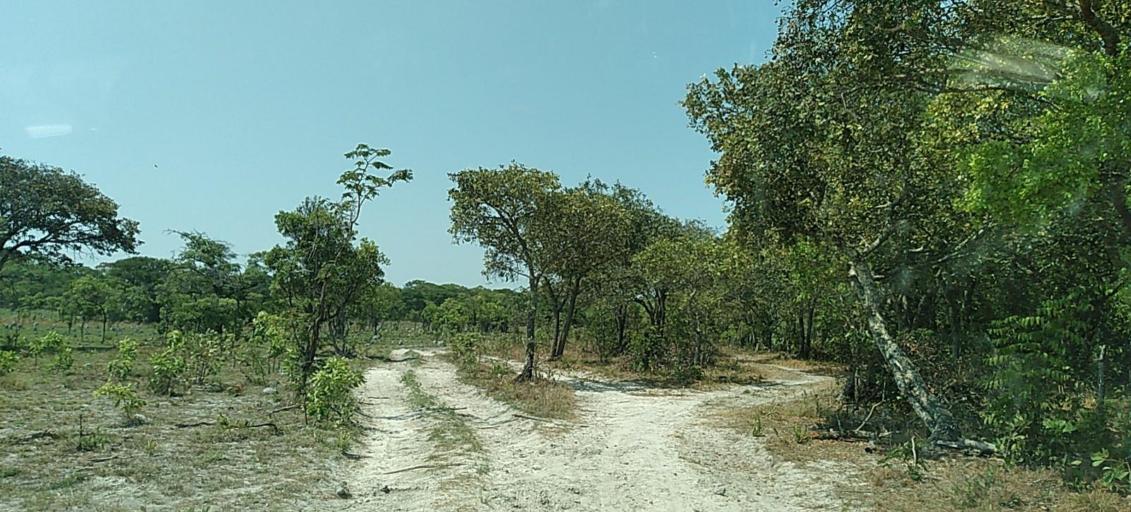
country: ZM
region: Copperbelt
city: Mpongwe
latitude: -13.7833
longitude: 28.1044
